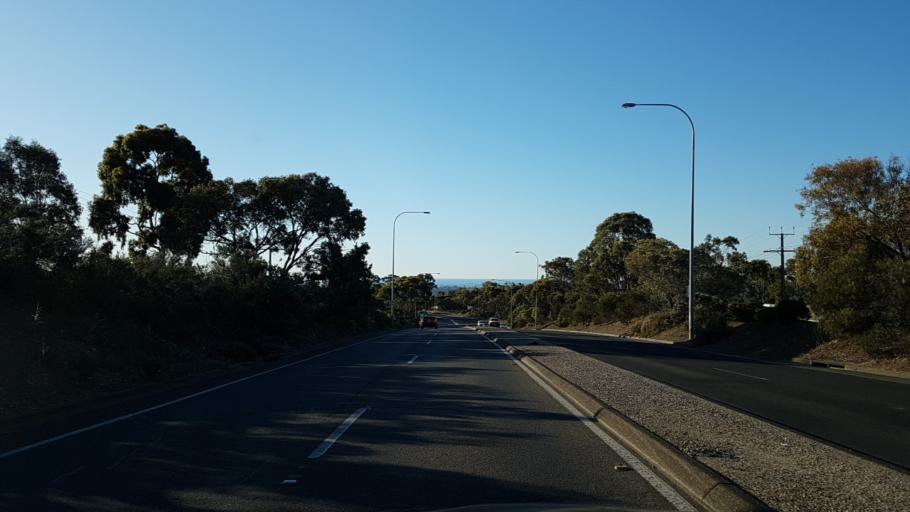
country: AU
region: South Australia
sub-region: Onkaparinga
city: Bedford Park
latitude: -35.0397
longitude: 138.5683
